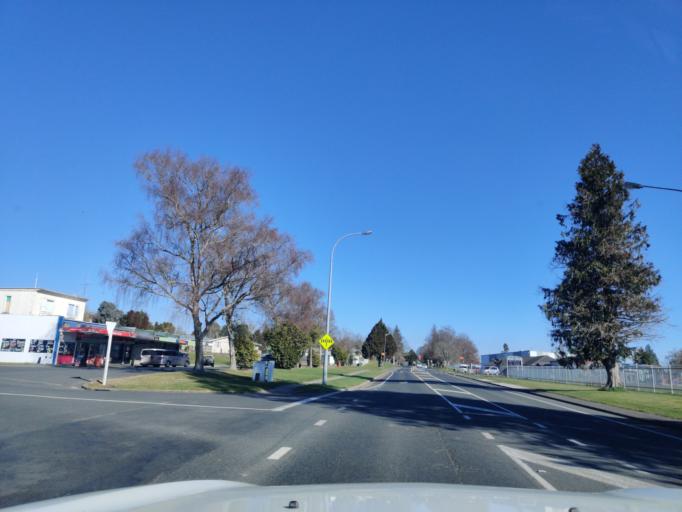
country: NZ
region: Waikato
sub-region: South Waikato District
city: Tokoroa
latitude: -38.2288
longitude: 175.8645
